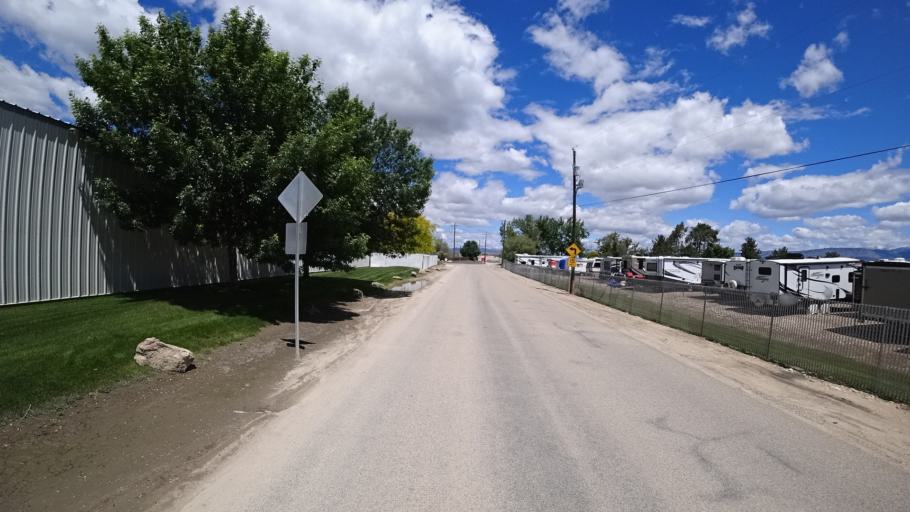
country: US
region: Idaho
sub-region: Ada County
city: Eagle
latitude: 43.6621
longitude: -116.3193
